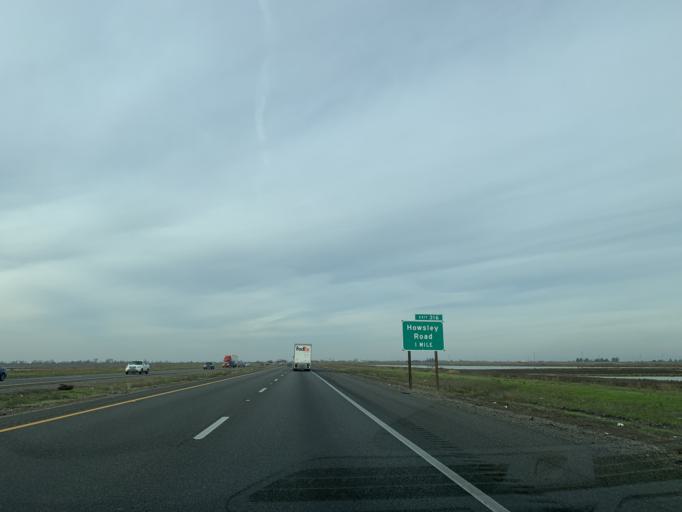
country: US
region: California
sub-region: Sacramento County
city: Elverta
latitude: 38.7981
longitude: -121.5436
